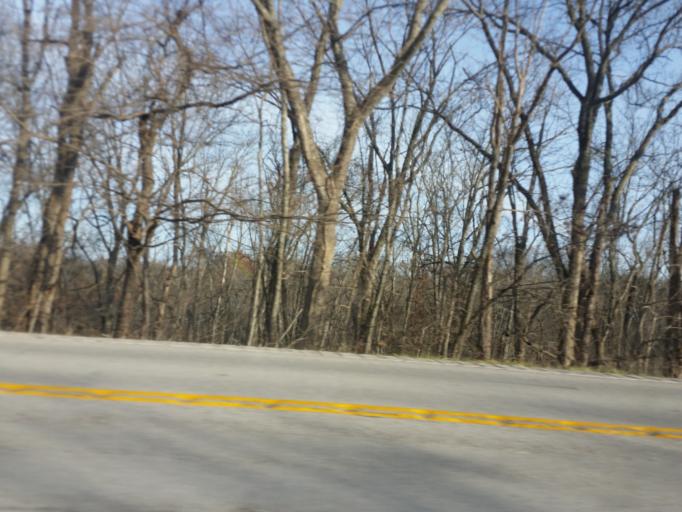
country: US
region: Kentucky
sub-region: Harrison County
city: Cynthiana
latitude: 38.4812
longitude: -84.2843
